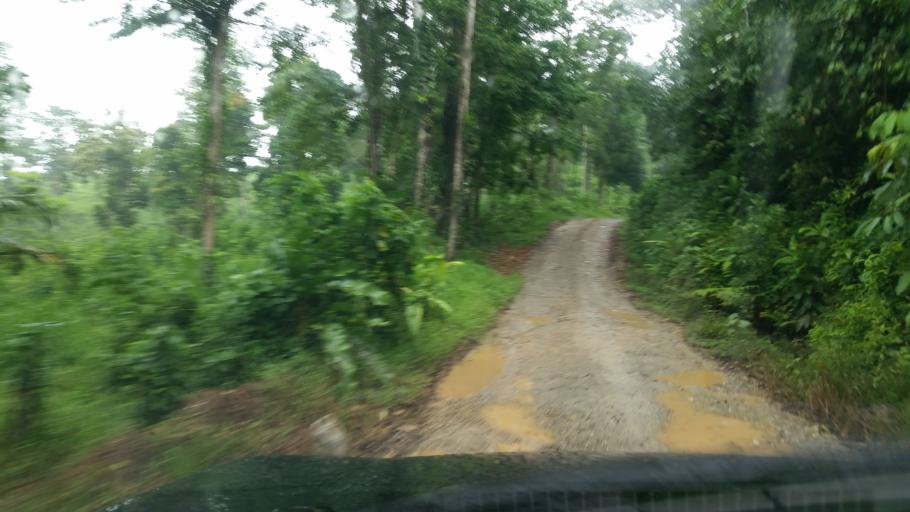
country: NI
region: Atlantico Norte (RAAN)
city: Bonanza
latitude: 14.0789
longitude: -84.6686
